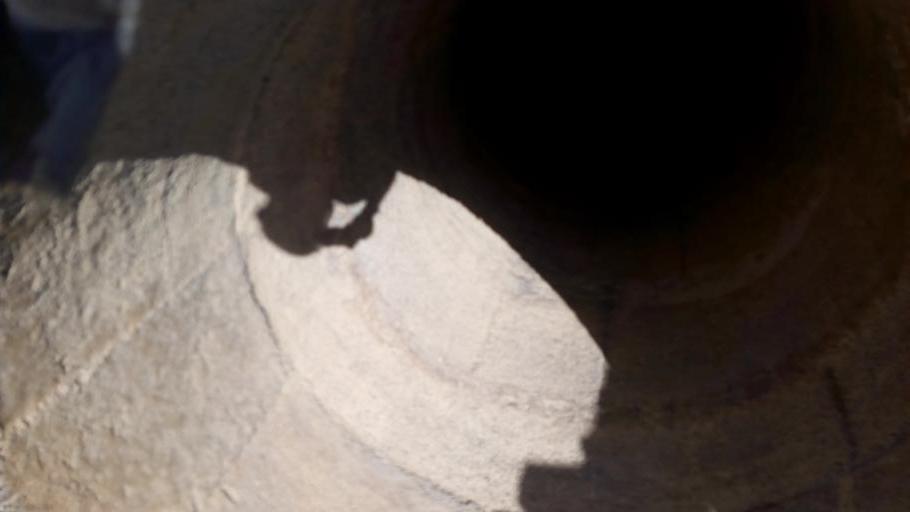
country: ML
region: Kayes
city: Diema
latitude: 14.5135
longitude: -8.8406
